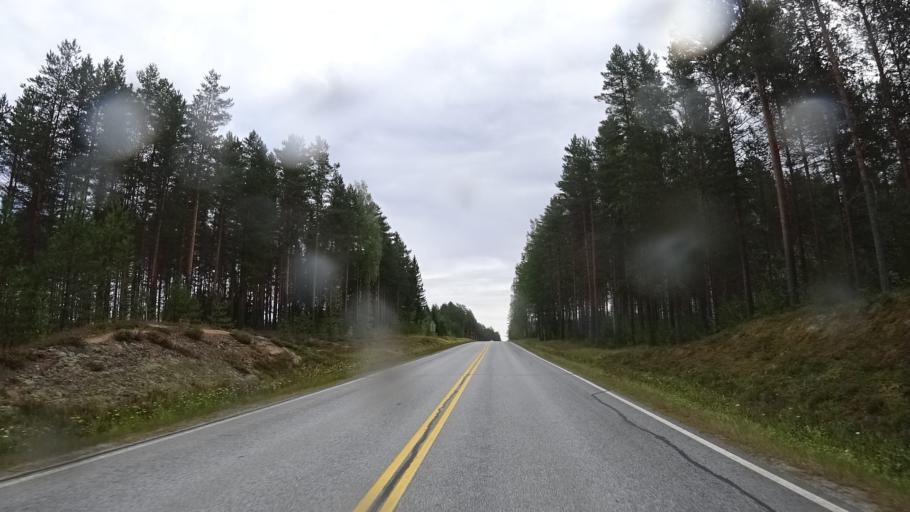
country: FI
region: North Karelia
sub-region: Keski-Karjala
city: Raeaekkylae
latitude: 62.1107
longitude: 29.7215
